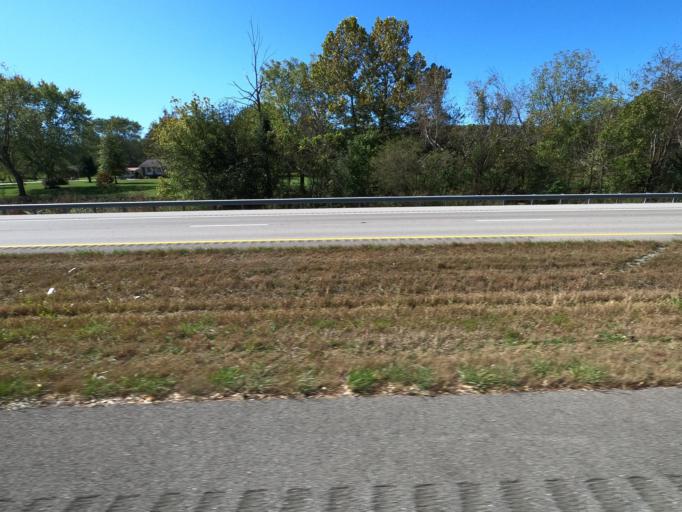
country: US
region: Tennessee
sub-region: Maury County
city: Mount Pleasant
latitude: 35.4005
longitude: -87.2793
